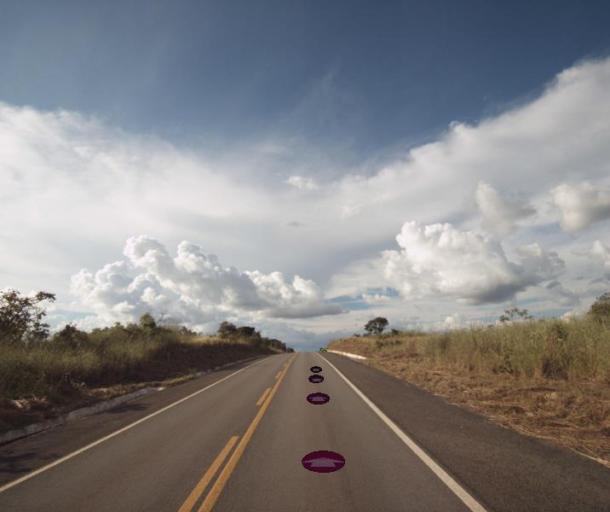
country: BR
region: Goias
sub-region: Barro Alto
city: Barro Alto
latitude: -14.8428
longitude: -48.6384
